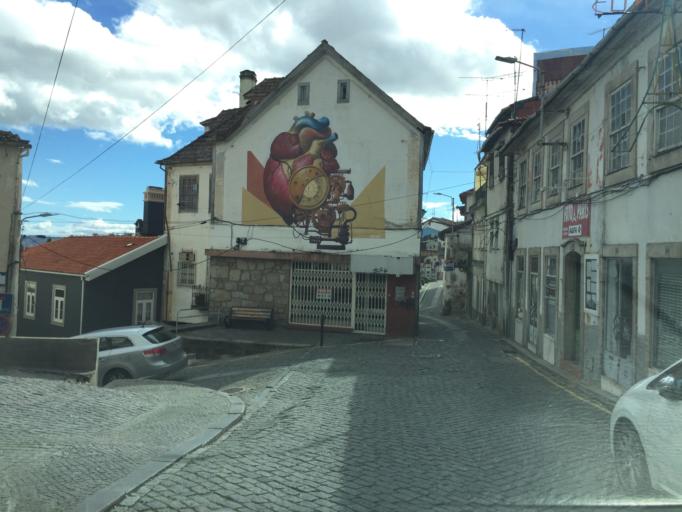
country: PT
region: Castelo Branco
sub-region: Covilha
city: Covilha
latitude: 40.2800
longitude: -7.5038
